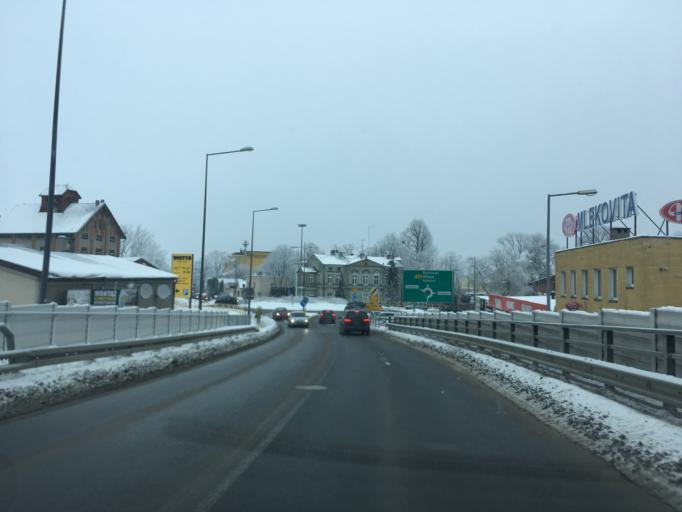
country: PL
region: Warmian-Masurian Voivodeship
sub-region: Powiat dzialdowski
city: Dzialdowo
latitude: 53.2359
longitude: 20.1701
